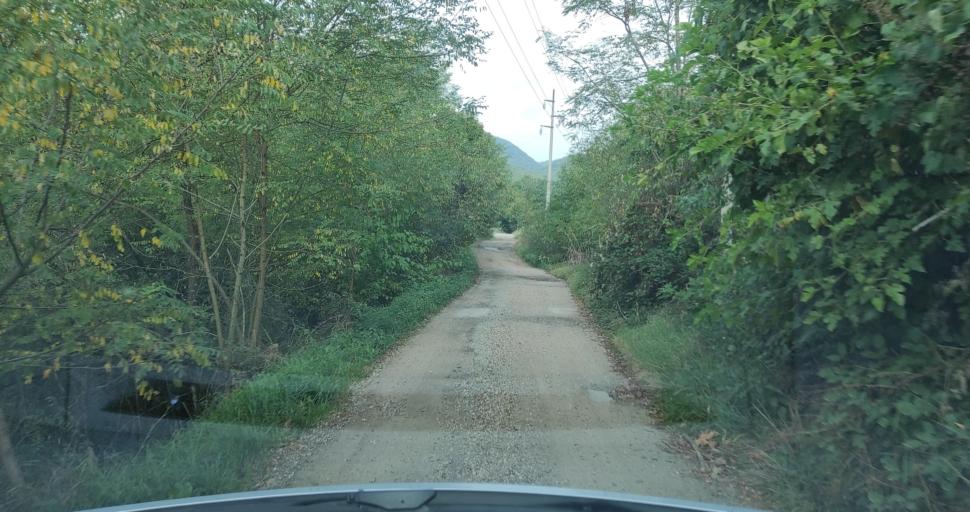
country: RS
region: Central Serbia
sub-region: Pcinjski Okrug
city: Vladicin Han
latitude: 42.6759
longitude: 22.0112
